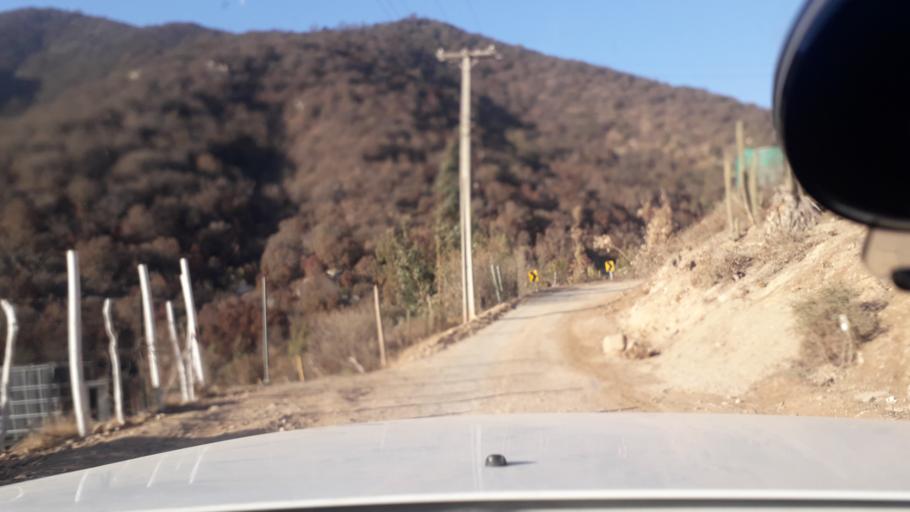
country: CL
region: Valparaiso
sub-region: Provincia de Marga Marga
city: Limache
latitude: -33.0518
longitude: -71.0784
